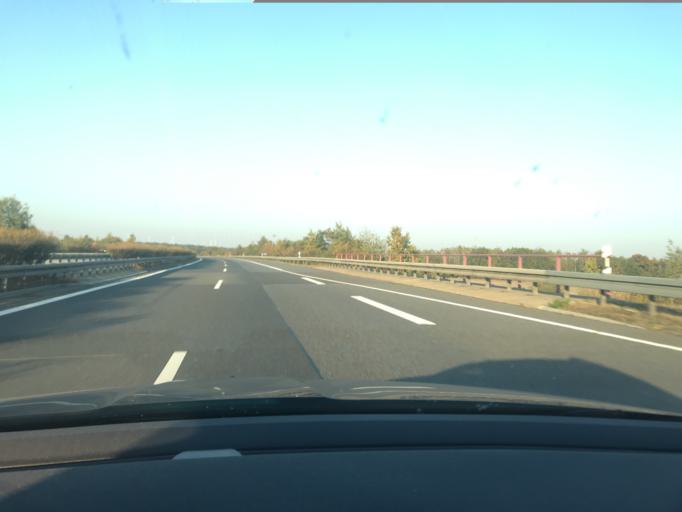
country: DE
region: Brandenburg
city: Schipkau
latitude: 51.5629
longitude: 13.9248
